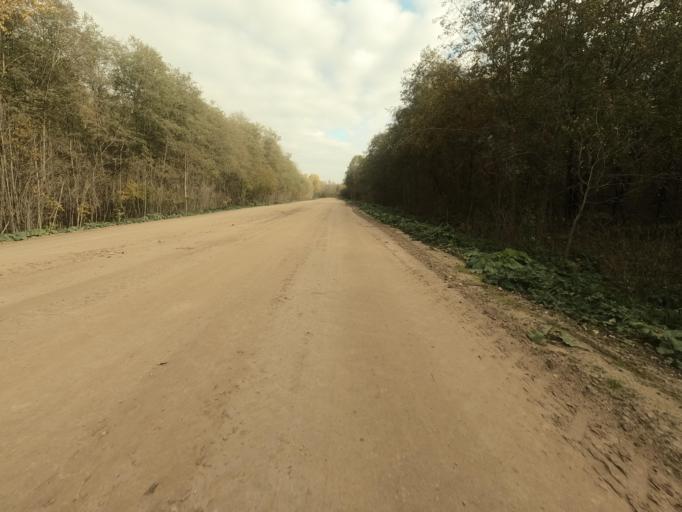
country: RU
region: Novgorod
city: Batetskiy
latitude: 58.7999
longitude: 30.6410
